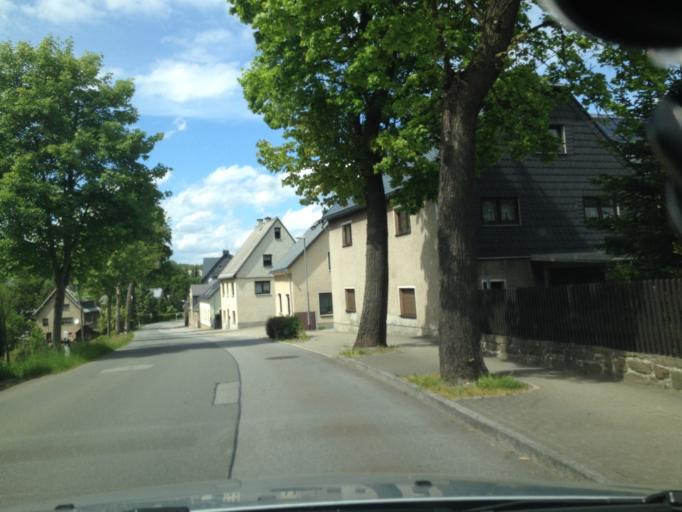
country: DE
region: Saxony
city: Barenstein
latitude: 50.5266
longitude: 12.9960
